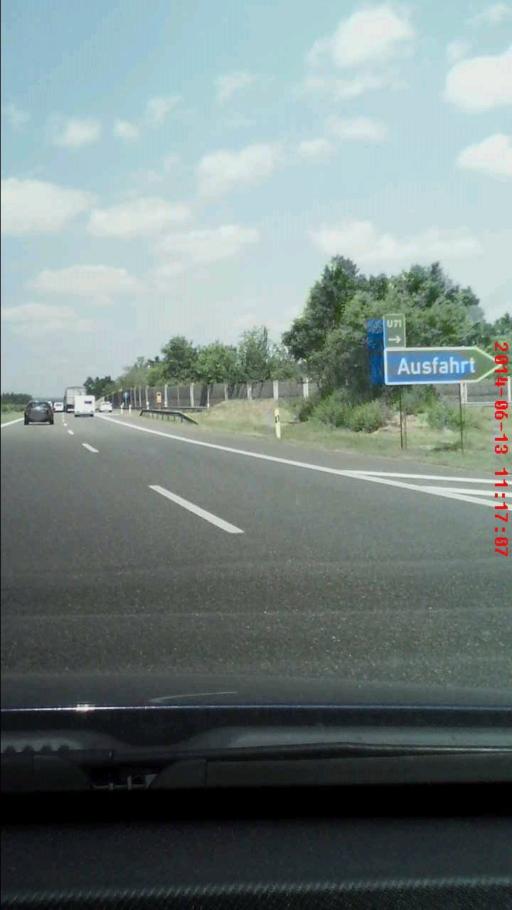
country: DE
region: Bavaria
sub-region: Upper Palatinate
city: Weiden
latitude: 49.6678
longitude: 12.1365
